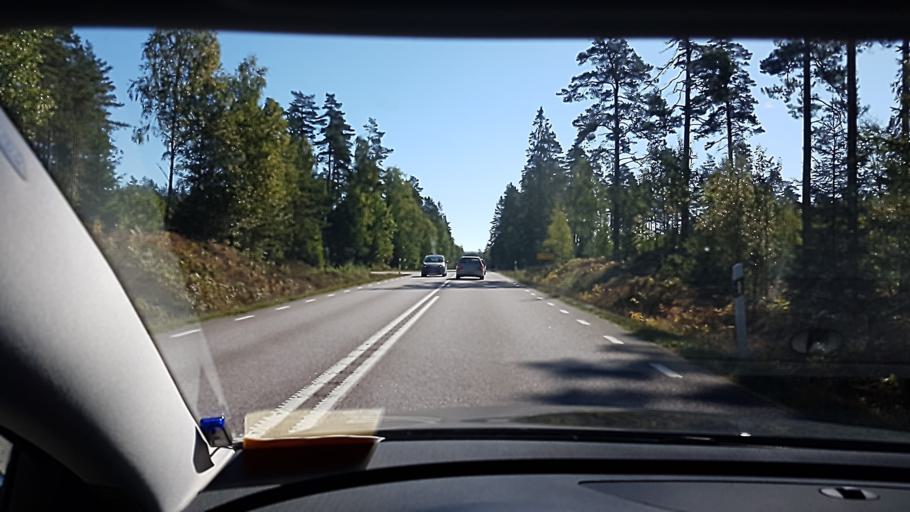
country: SE
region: Kronoberg
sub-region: Lessebo Kommun
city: Hovmantorp
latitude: 56.7857
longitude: 15.1881
